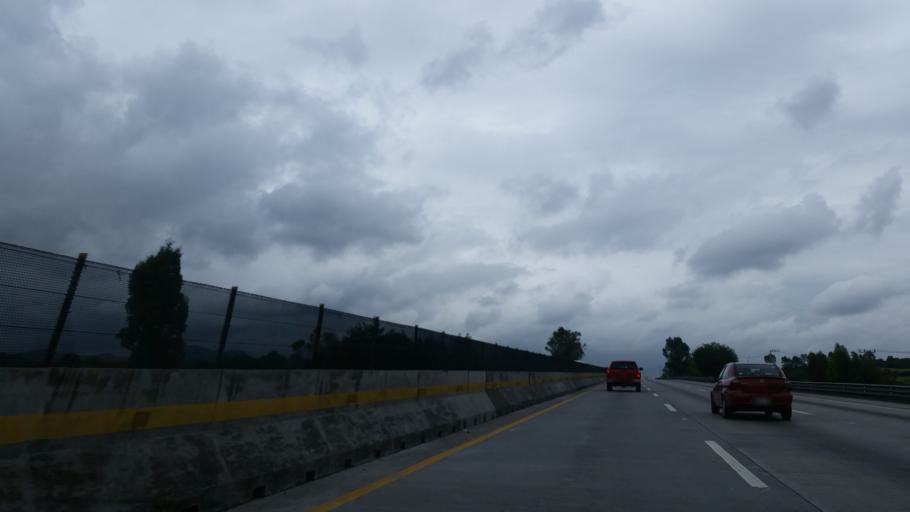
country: MX
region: Hidalgo
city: Tepeji de Ocampo
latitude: 19.9243
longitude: -99.3736
